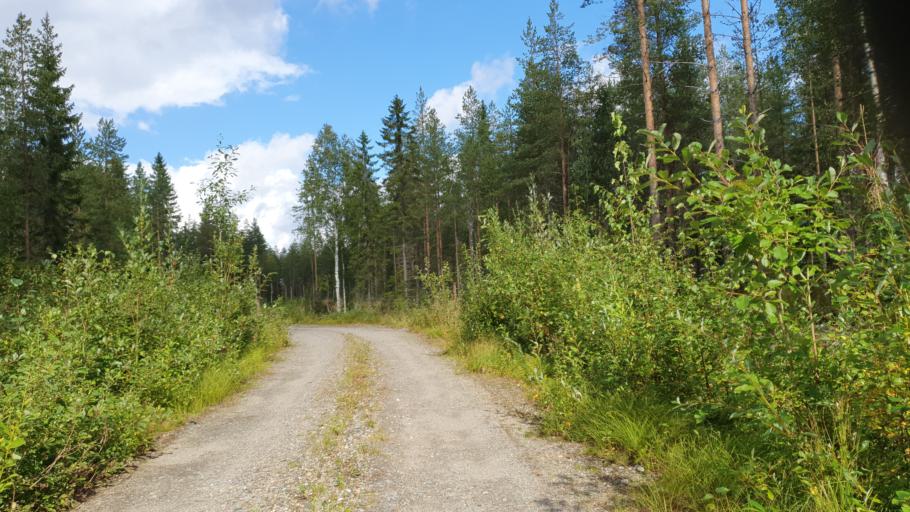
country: FI
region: Kainuu
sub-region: Kehys-Kainuu
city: Kuhmo
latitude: 64.1412
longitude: 29.3871
